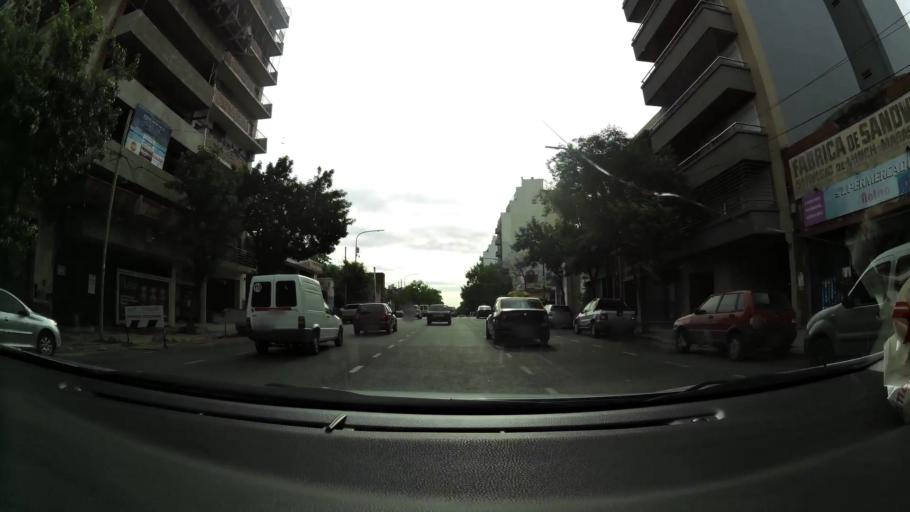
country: AR
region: Buenos Aires F.D.
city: Buenos Aires
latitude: -34.6316
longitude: -58.4171
